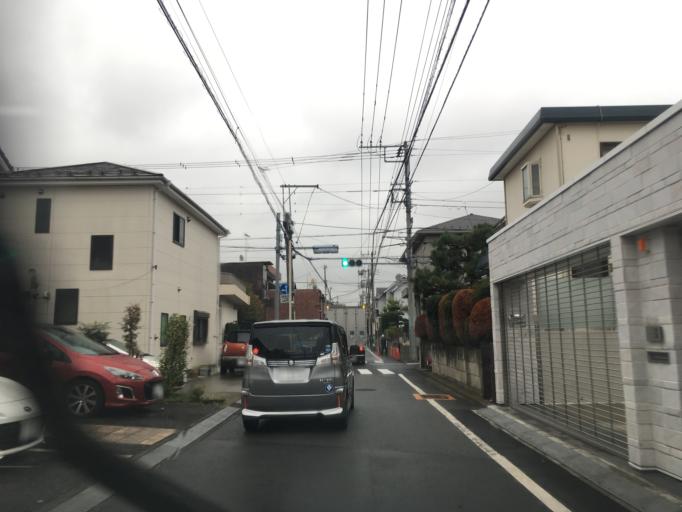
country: JP
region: Tokyo
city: Kokubunji
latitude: 35.6976
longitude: 139.4410
